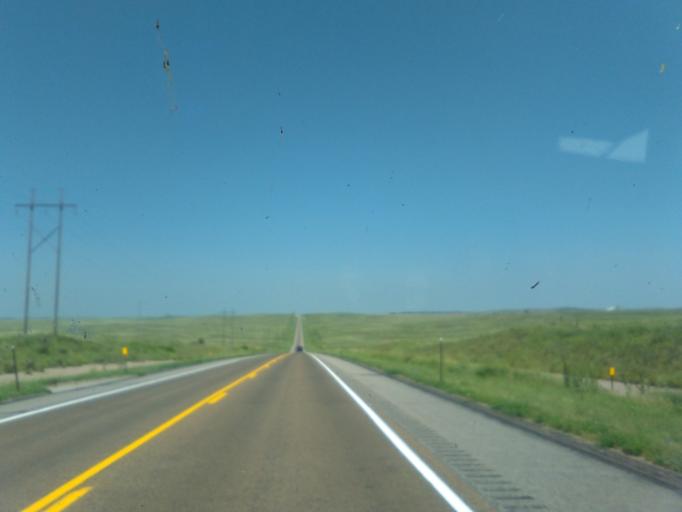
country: US
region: Nebraska
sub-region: Lincoln County
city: North Platte
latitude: 40.8484
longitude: -100.7540
